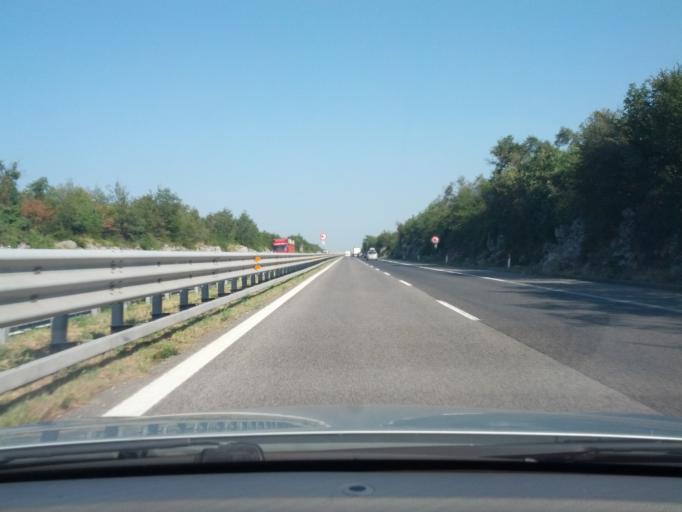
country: IT
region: Friuli Venezia Giulia
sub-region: Provincia di Trieste
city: Prosecco-Contovello
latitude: 45.7208
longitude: 13.7260
